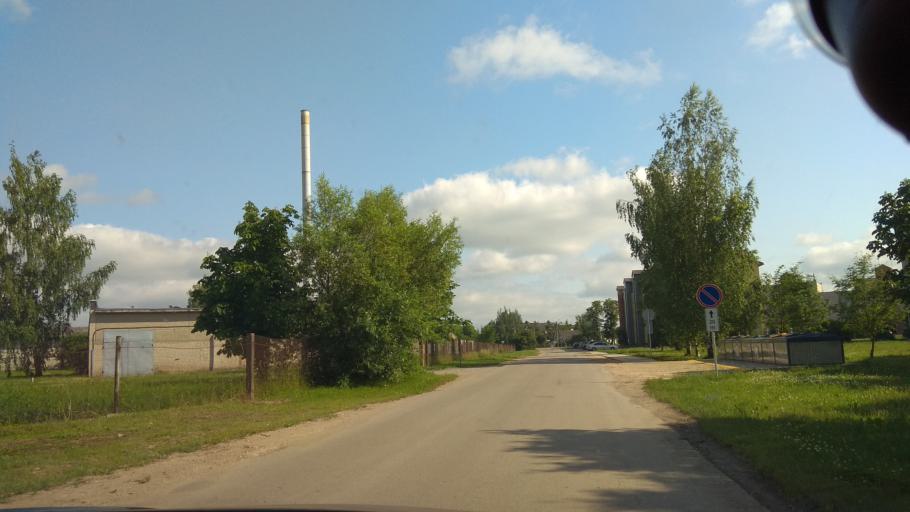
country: LT
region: Siauliu apskritis
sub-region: Joniskis
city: Joniskis
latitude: 56.2435
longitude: 23.6280
